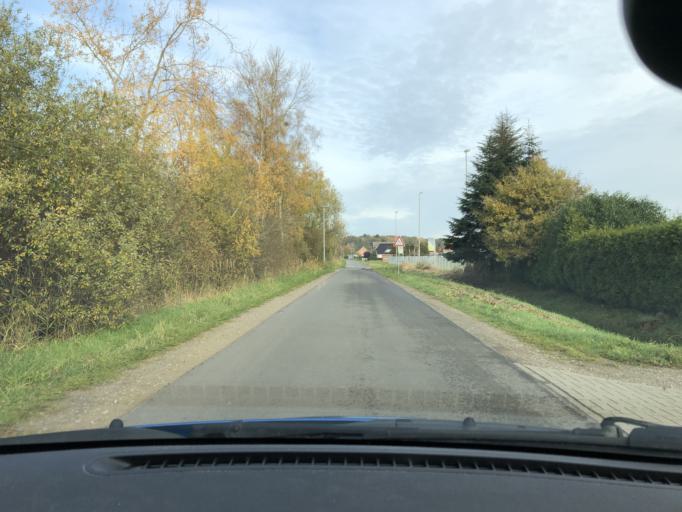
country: DE
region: Lower Saxony
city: Artlenburg
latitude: 53.3719
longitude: 10.4804
